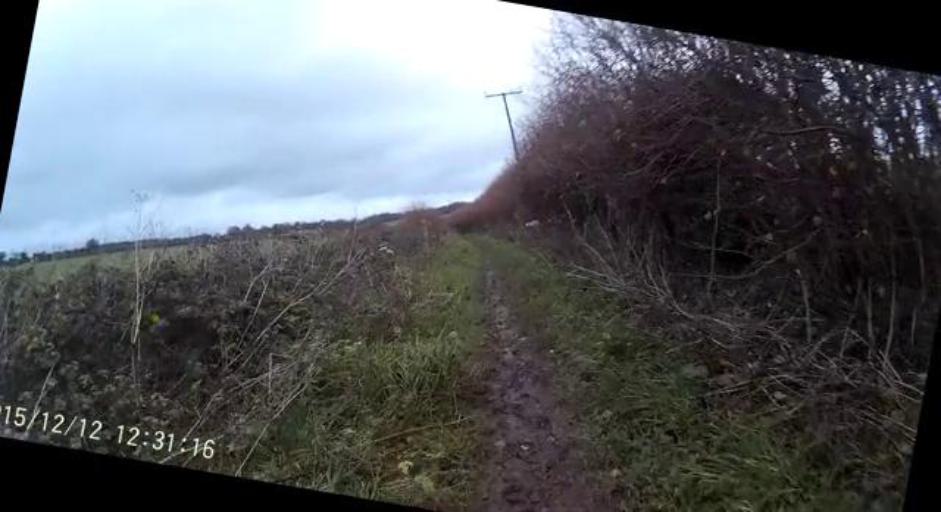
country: GB
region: England
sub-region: Hampshire
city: Cowplain
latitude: 50.9482
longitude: -0.9921
